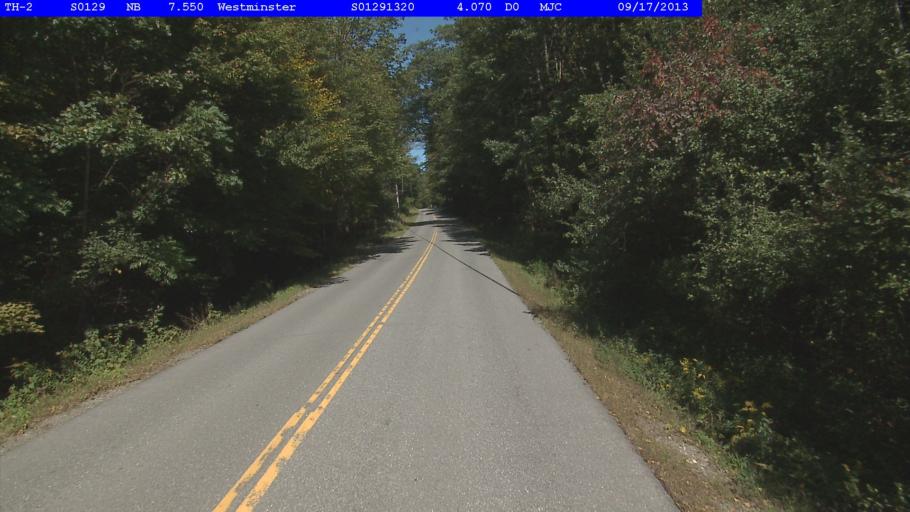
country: US
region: Vermont
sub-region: Windham County
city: Bellows Falls
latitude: 43.0740
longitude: -72.5391
